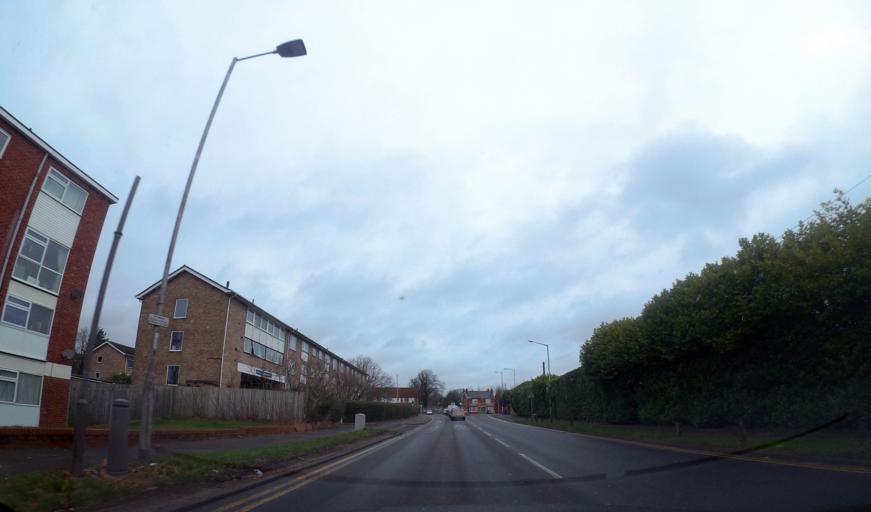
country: GB
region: England
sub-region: West Berkshire
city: Tilehurst
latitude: 51.4432
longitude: -1.0192
